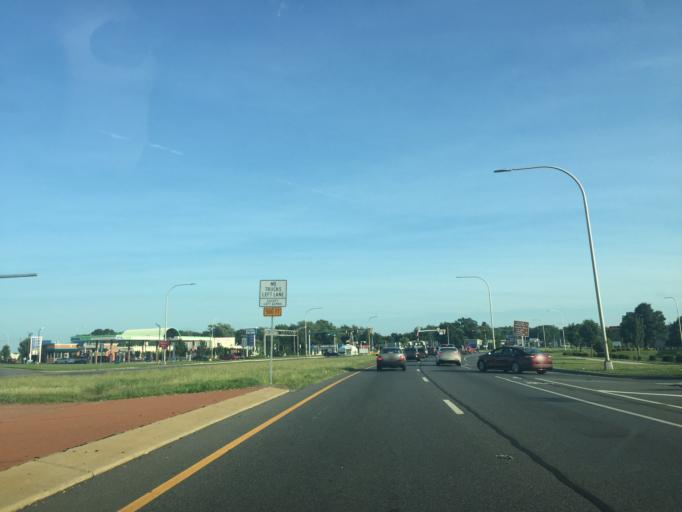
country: US
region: Delaware
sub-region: Kent County
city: Dover
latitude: 39.1591
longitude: -75.5123
